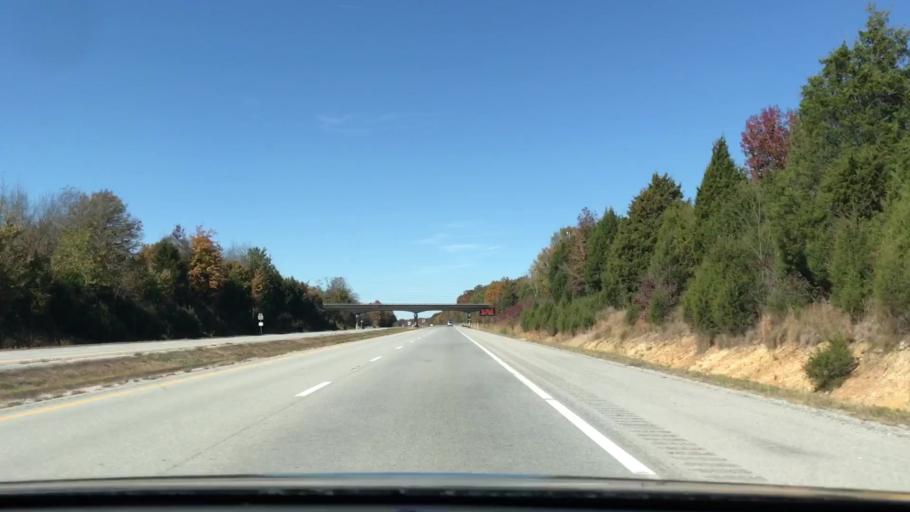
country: US
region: Kentucky
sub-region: Barren County
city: Cave City
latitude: 37.0362
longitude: -86.0578
